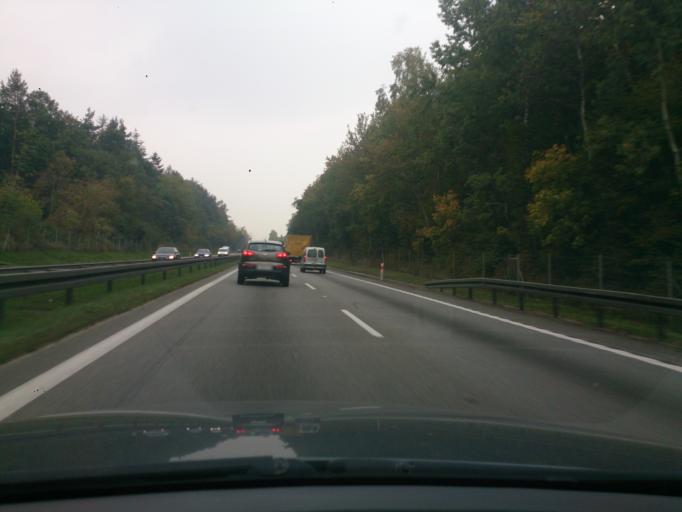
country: PL
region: Pomeranian Voivodeship
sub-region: Gdynia
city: Wielki Kack
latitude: 54.3894
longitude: 18.4954
